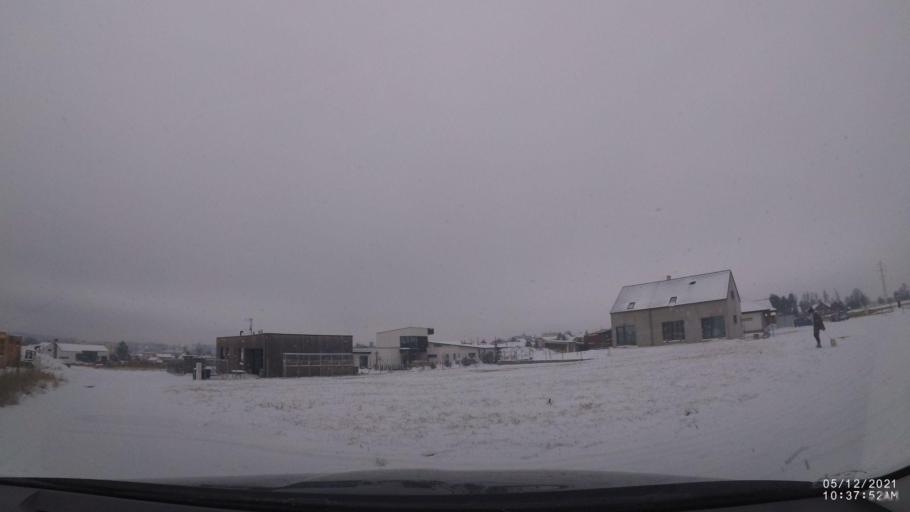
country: CZ
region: Kralovehradecky
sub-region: Okres Rychnov nad Kneznou
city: Rychnov nad Kneznou
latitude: 50.1662
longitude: 16.2919
